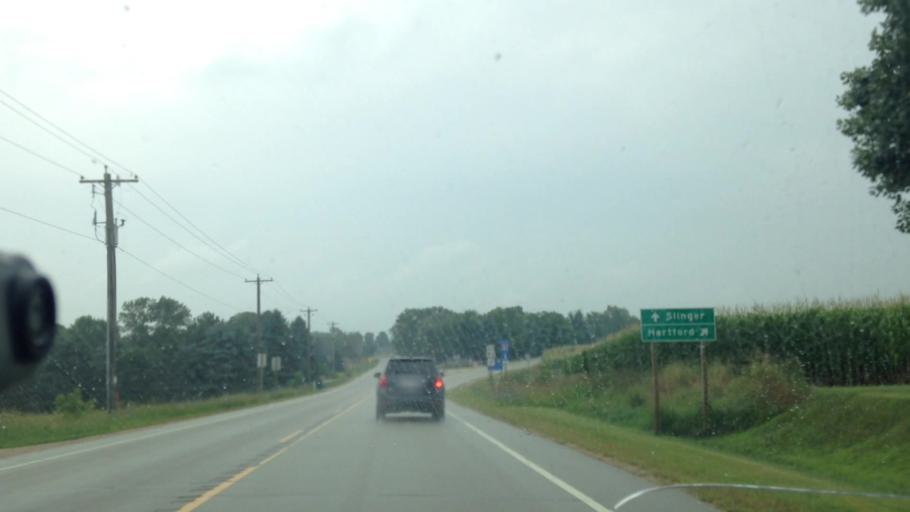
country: US
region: Wisconsin
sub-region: Washington County
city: Hartford
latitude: 43.3872
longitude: -88.3538
